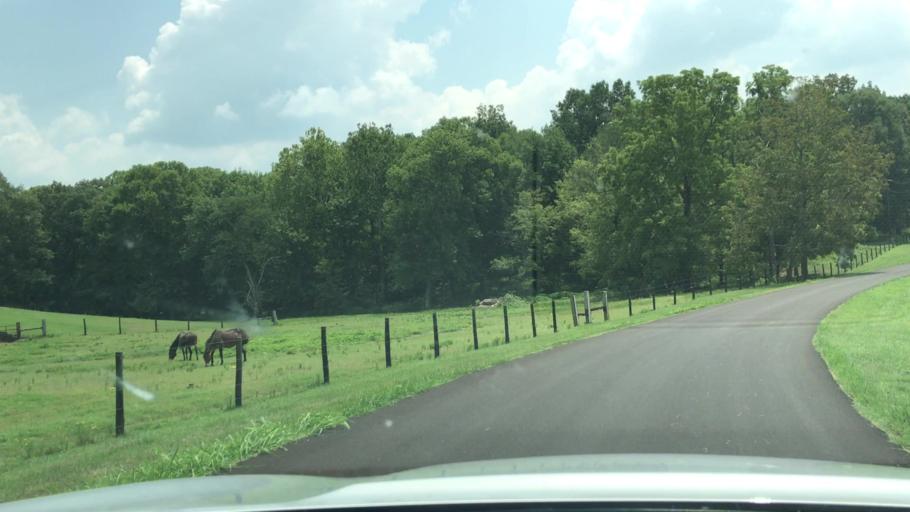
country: US
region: Kentucky
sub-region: Todd County
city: Elkton
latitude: 36.7740
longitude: -87.1418
